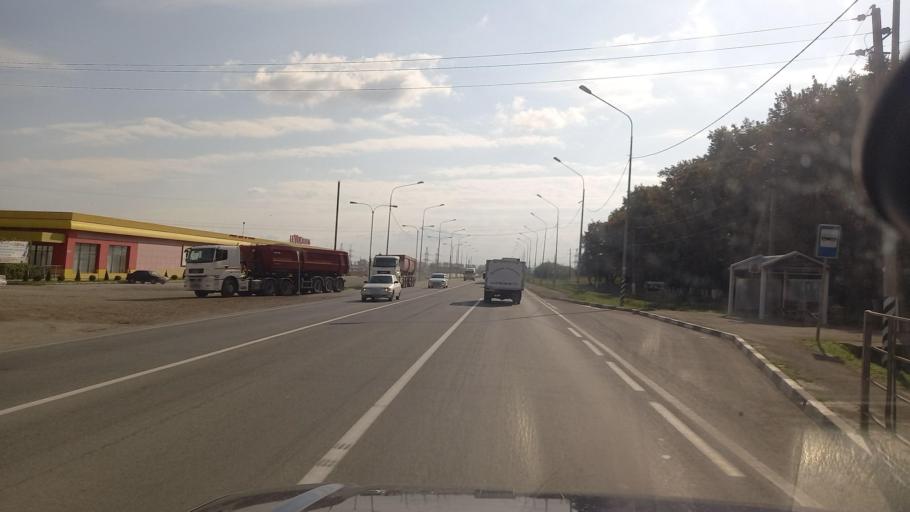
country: RU
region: Krasnodarskiy
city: Novoukrainskiy
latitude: 44.9087
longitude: 38.0227
